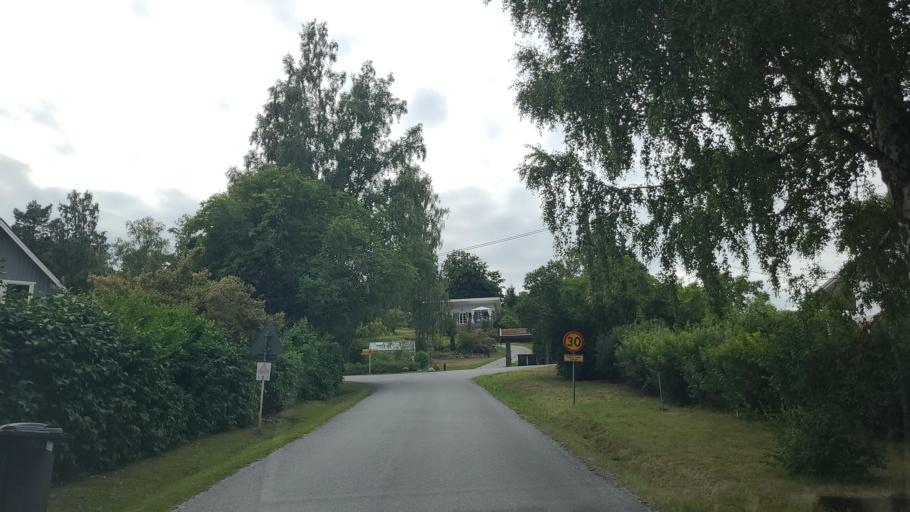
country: SE
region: Stockholm
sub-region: Upplands-Bro Kommun
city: Bro
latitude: 59.4759
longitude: 17.5586
